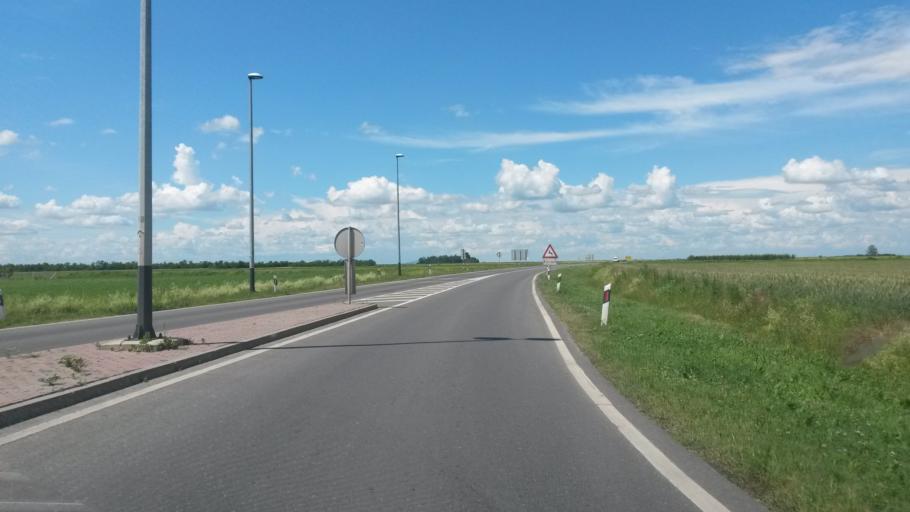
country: HR
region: Osjecko-Baranjska
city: Cepin
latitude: 45.5159
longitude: 18.5373
